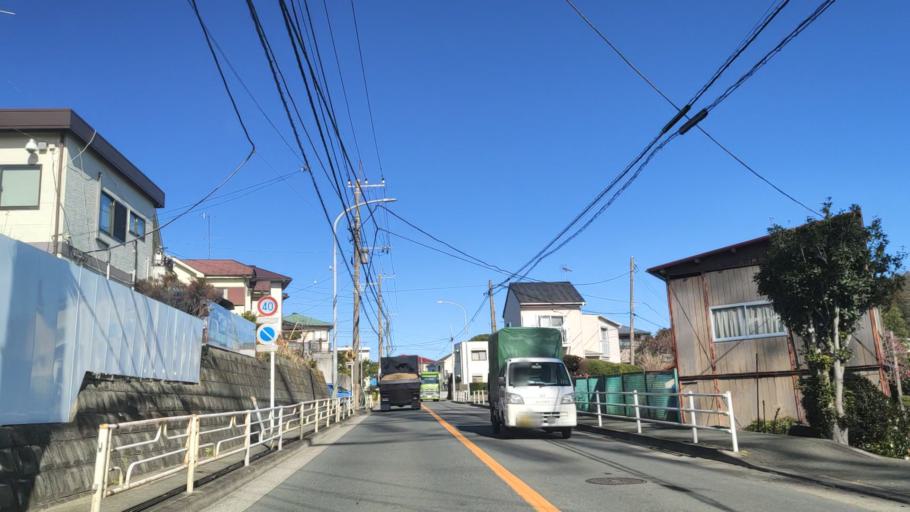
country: JP
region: Kanagawa
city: Minami-rinkan
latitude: 35.4929
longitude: 139.5167
